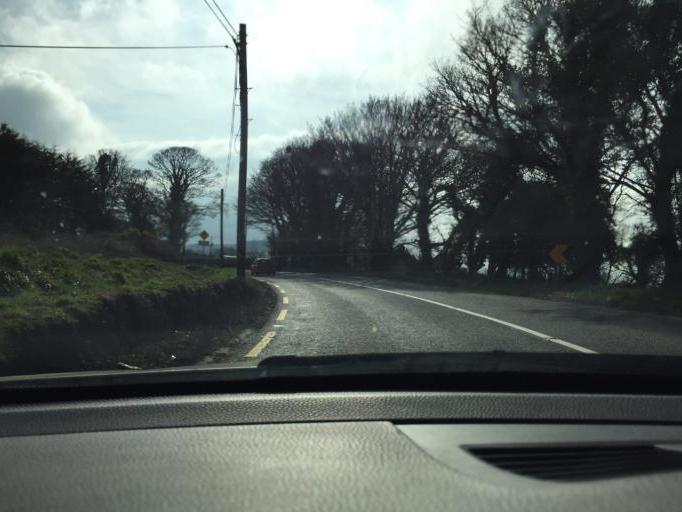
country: IE
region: Leinster
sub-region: South Dublin
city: Saggart
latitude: 53.2733
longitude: -6.4304
